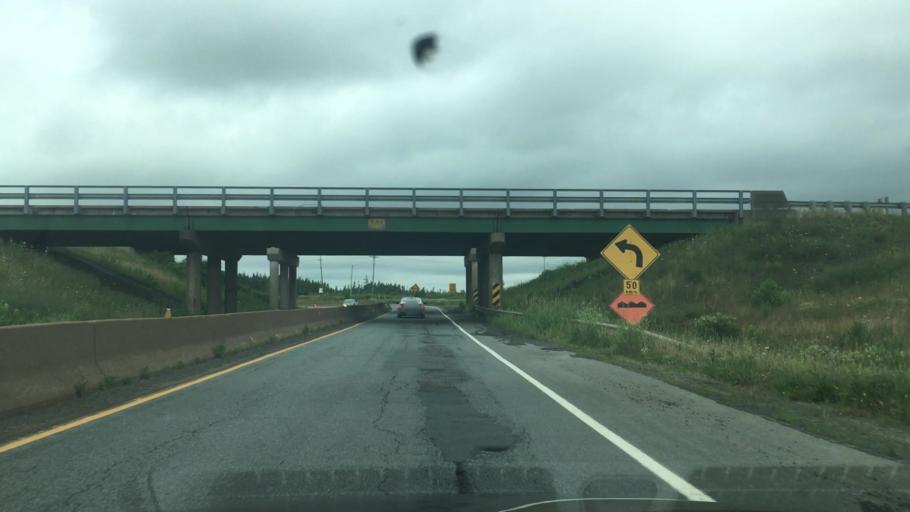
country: CA
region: Nova Scotia
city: Truro
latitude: 45.3897
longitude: -63.3244
